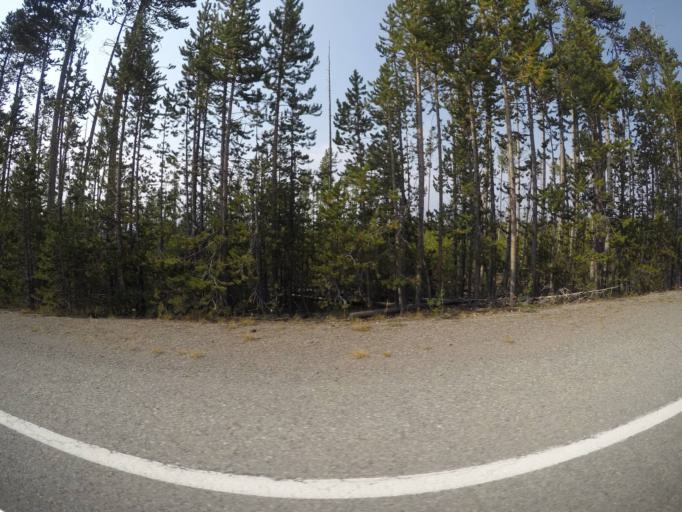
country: US
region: Montana
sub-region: Gallatin County
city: West Yellowstone
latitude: 44.7195
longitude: -110.6514
